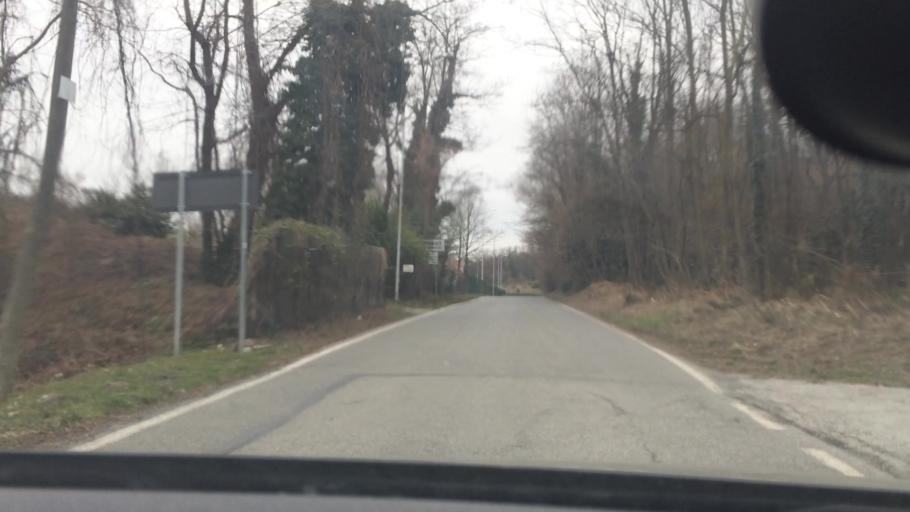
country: IT
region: Lombardy
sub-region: Provincia di Como
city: Arosio
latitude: 45.7300
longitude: 9.2056
